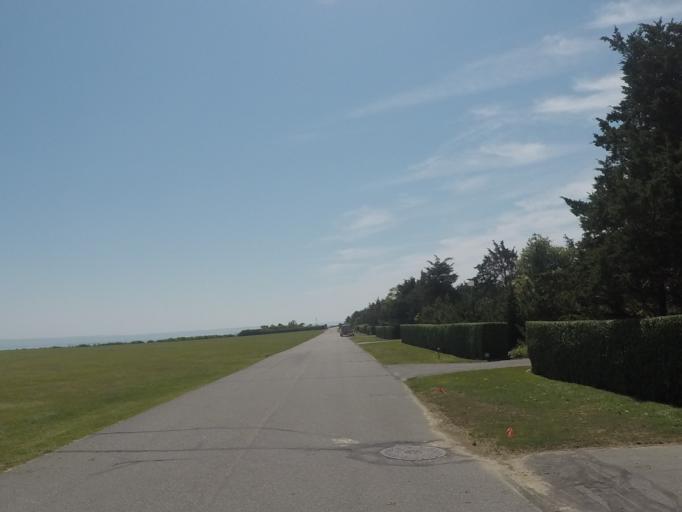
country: US
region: Massachusetts
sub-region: Bristol County
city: Bliss Corner
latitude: 41.5423
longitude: -70.9333
